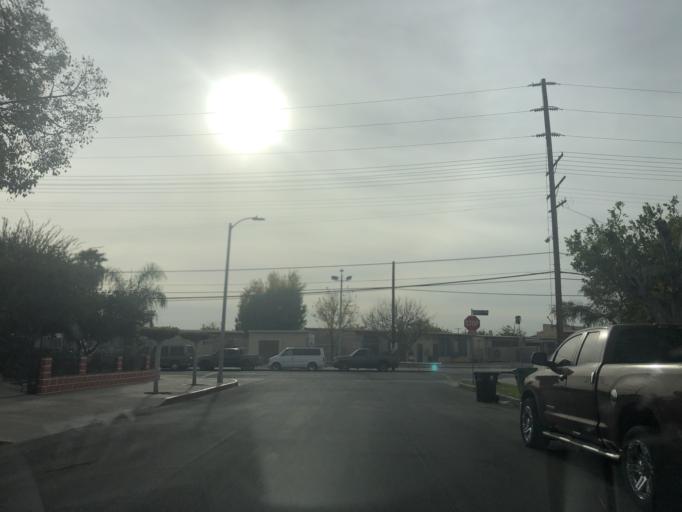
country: US
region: California
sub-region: Los Angeles County
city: San Fernando
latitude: 34.2692
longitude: -118.4308
